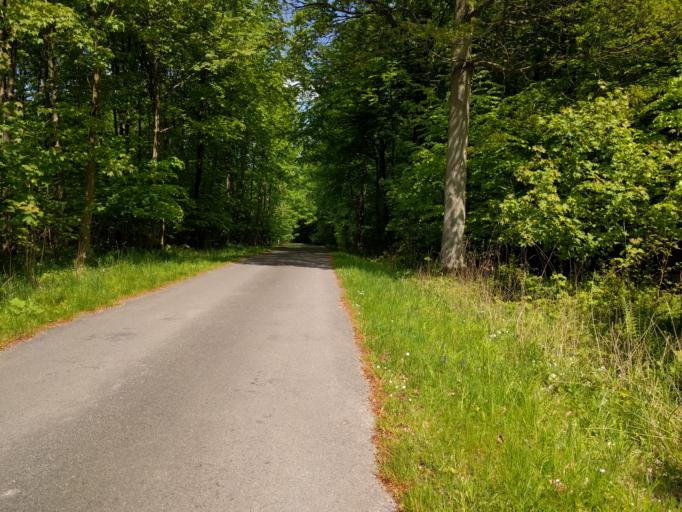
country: DK
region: Zealand
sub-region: Guldborgsund Kommune
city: Stubbekobing
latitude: 54.7941
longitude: 12.0899
